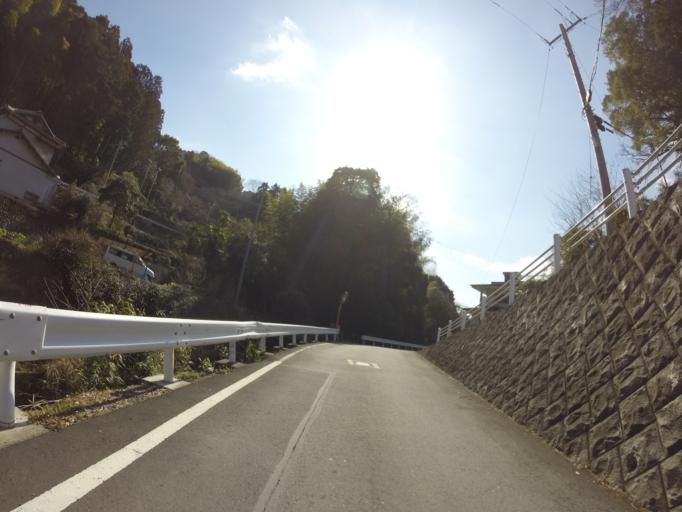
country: JP
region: Shizuoka
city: Shizuoka-shi
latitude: 35.0766
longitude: 138.4945
